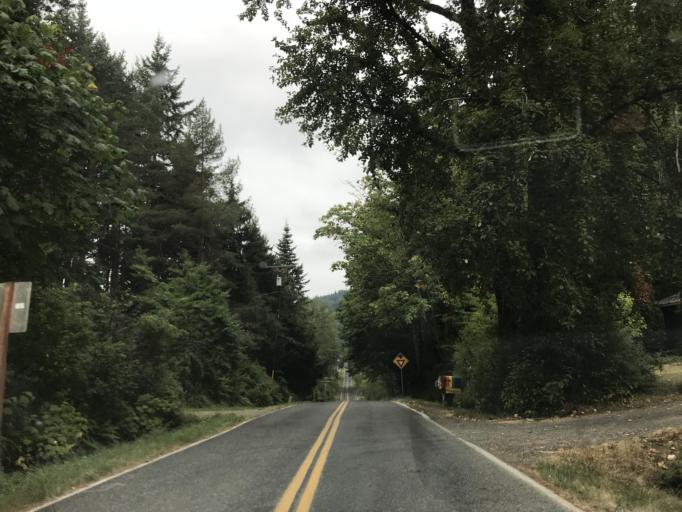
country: US
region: Washington
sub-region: Whatcom County
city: Sudden Valley
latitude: 48.7749
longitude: -122.3421
